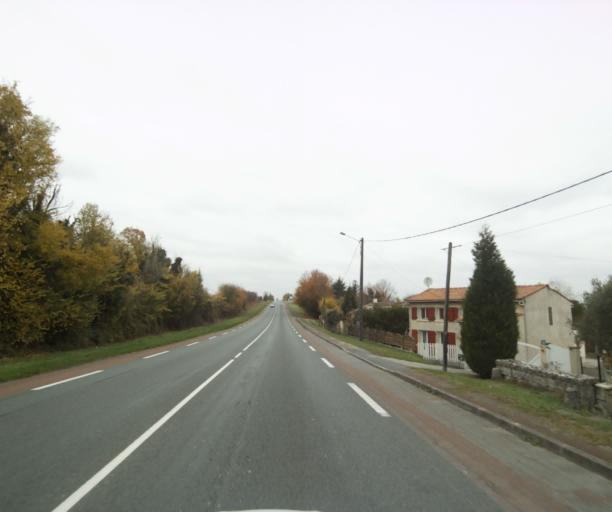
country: FR
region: Poitou-Charentes
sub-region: Departement de la Charente-Maritime
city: Les Gonds
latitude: 45.7140
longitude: -0.6326
